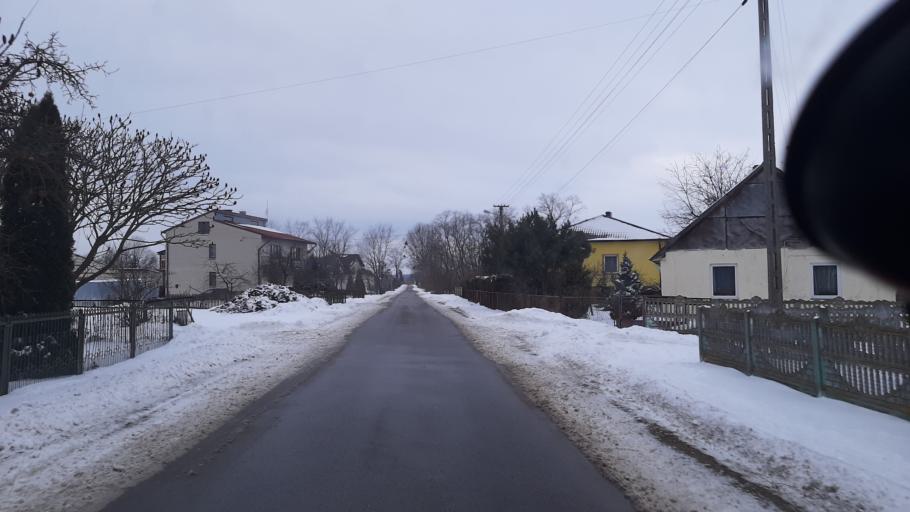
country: PL
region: Lublin Voivodeship
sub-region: Powiat lubartowski
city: Abramow
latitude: 51.4421
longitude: 22.2866
